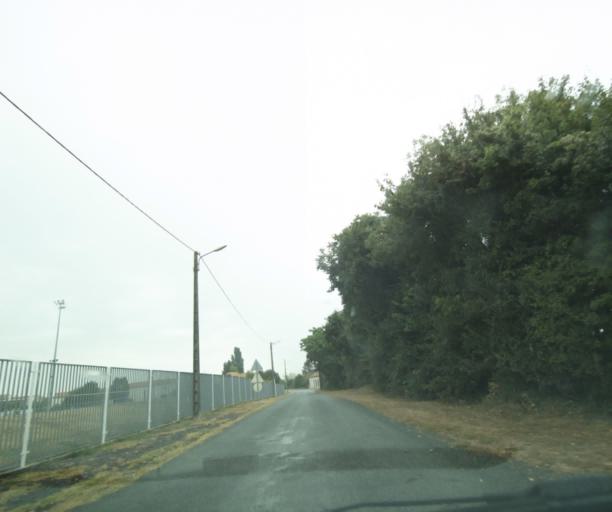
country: FR
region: Poitou-Charentes
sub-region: Departement de la Charente-Maritime
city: Tonnay-Charente
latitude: 45.9440
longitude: -0.9069
